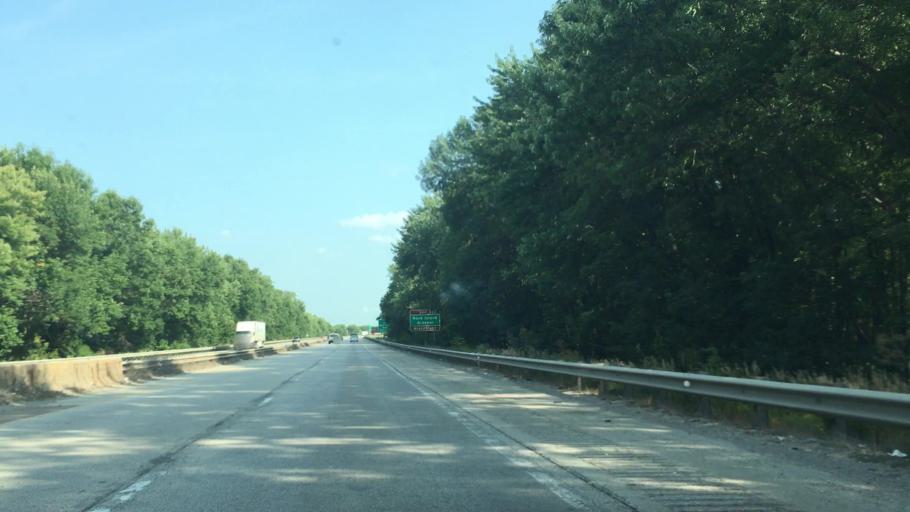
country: US
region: Illinois
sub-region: Rock Island County
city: Milan
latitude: 41.4729
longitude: -90.6245
